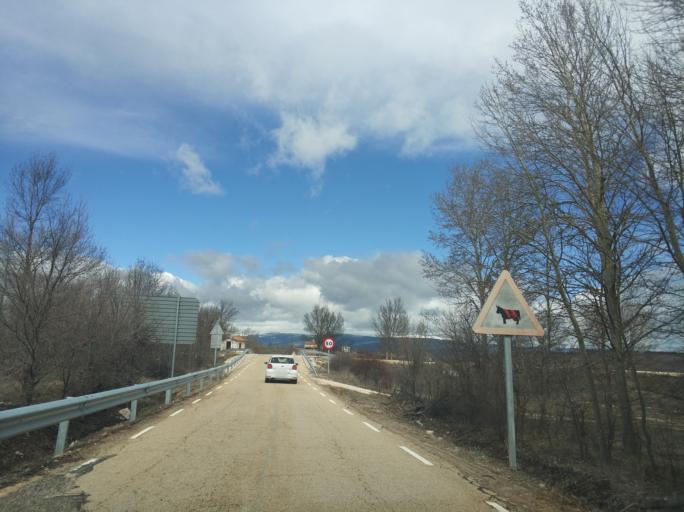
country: ES
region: Castille and Leon
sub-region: Provincia de Soria
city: Abejar
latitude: 41.8012
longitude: -2.7814
